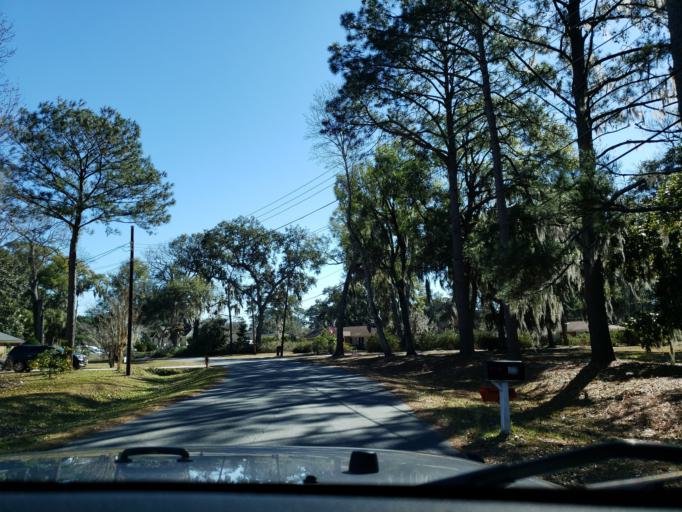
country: US
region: Georgia
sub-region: Chatham County
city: Wilmington Island
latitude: 32.0358
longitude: -80.9696
